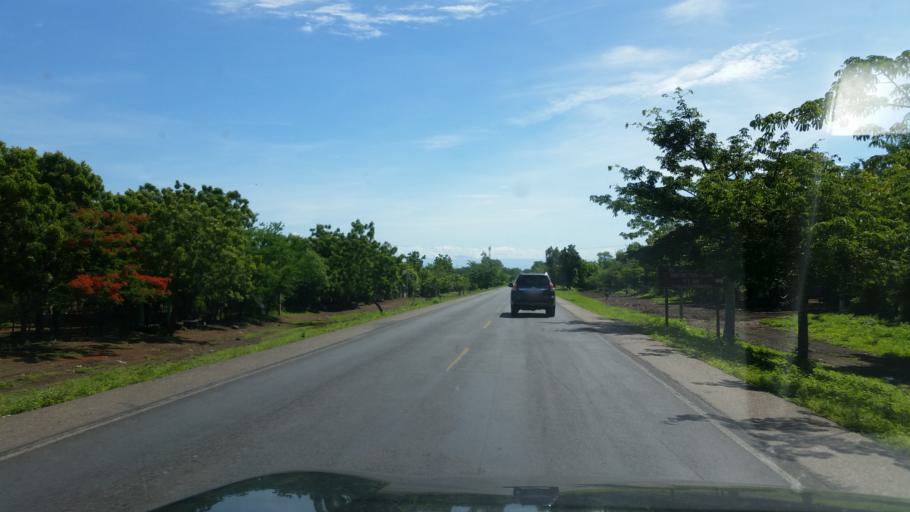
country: NI
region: Chinandega
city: El Viejo
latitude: 12.7594
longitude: -87.0628
